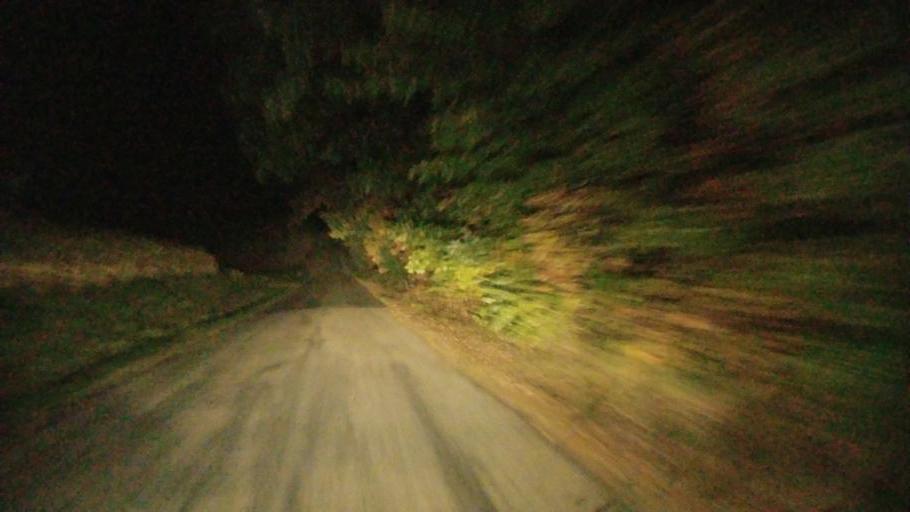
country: US
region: Ohio
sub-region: Ashland County
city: Loudonville
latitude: 40.5899
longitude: -82.3569
